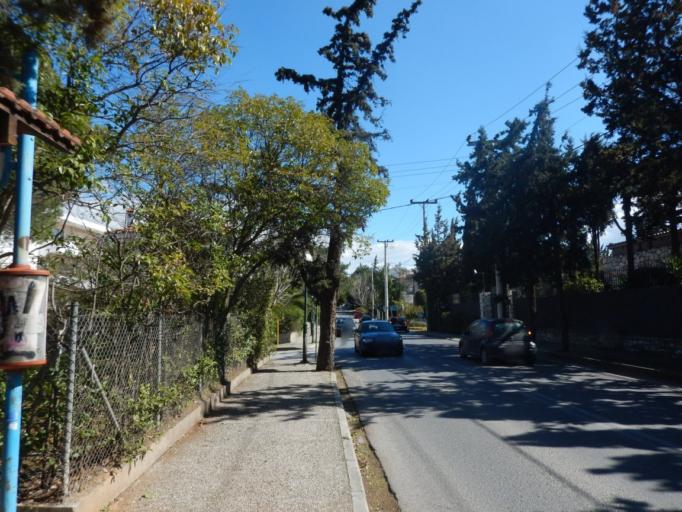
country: GR
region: Attica
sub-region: Nomarchia Athinas
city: Kifisia
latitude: 38.0664
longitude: 23.8258
